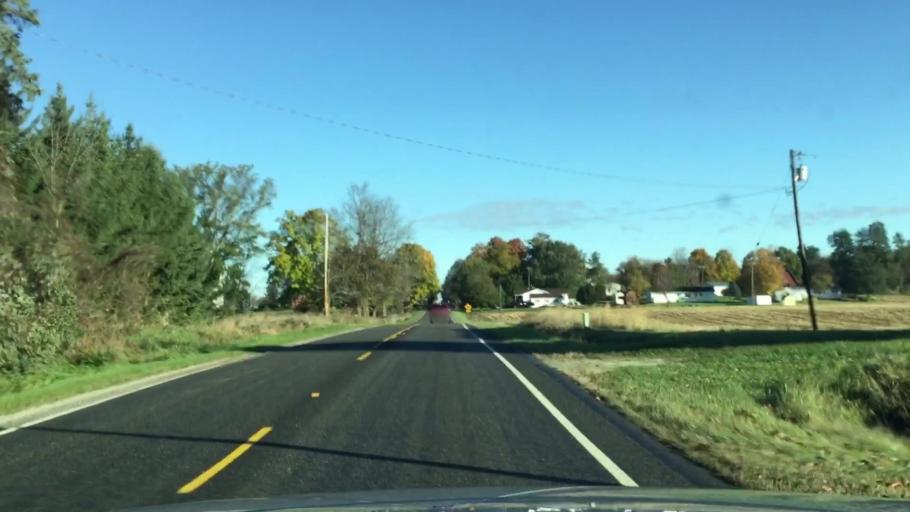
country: US
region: Michigan
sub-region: Shiawassee County
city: Durand
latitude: 42.8358
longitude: -83.9450
